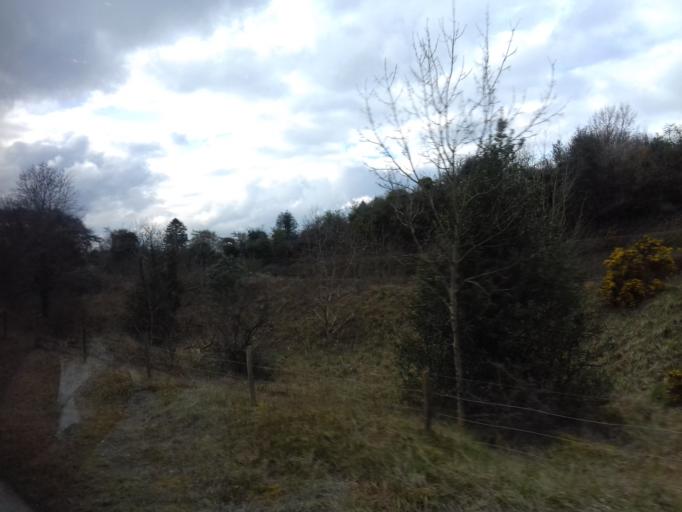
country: IE
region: Leinster
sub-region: An Iarmhi
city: Rathwire
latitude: 53.4951
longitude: -7.1752
